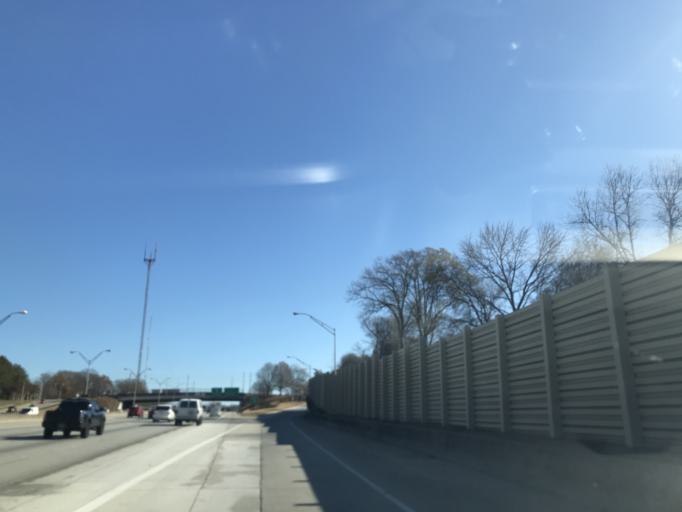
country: US
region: Georgia
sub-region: Fulton County
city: Atlanta
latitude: 33.7427
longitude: -84.3711
